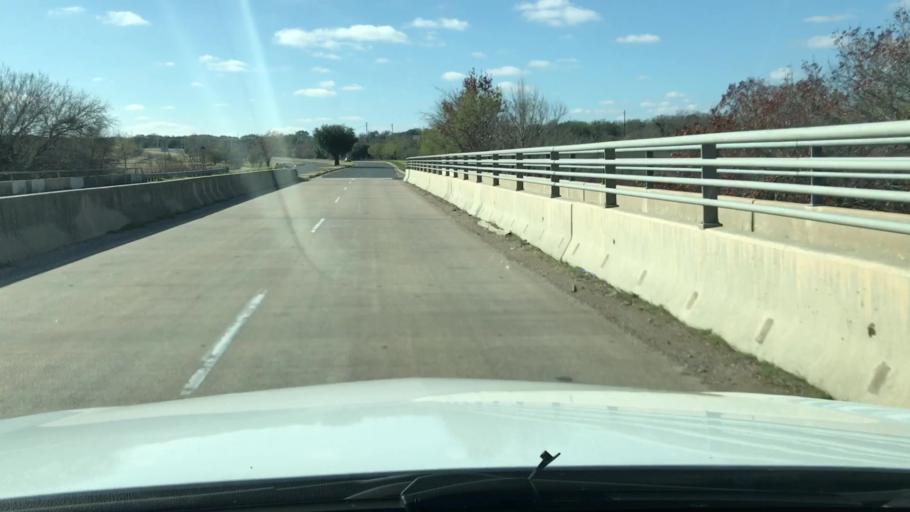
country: US
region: Texas
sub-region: Travis County
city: Onion Creek
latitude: 30.1843
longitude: -97.7177
